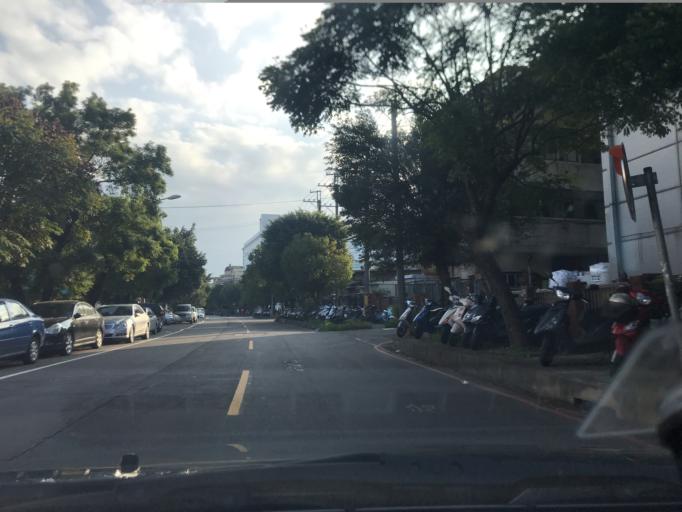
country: TW
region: Taiwan
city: Taoyuan City
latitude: 24.9828
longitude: 121.2351
